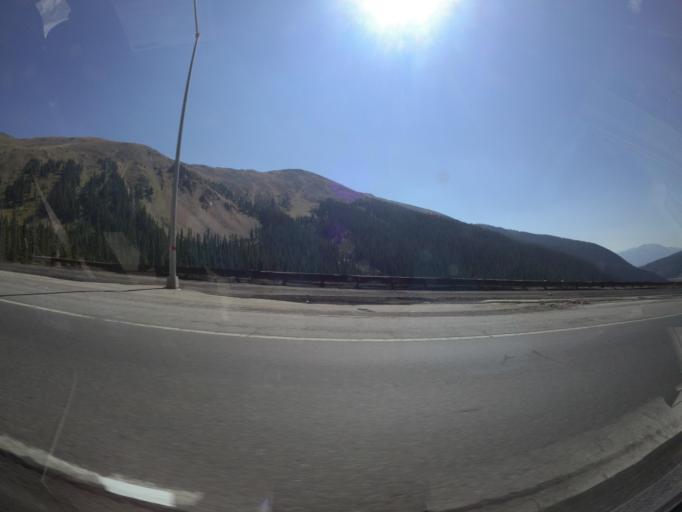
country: US
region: Colorado
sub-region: Summit County
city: Keystone
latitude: 39.6778
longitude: -105.9451
